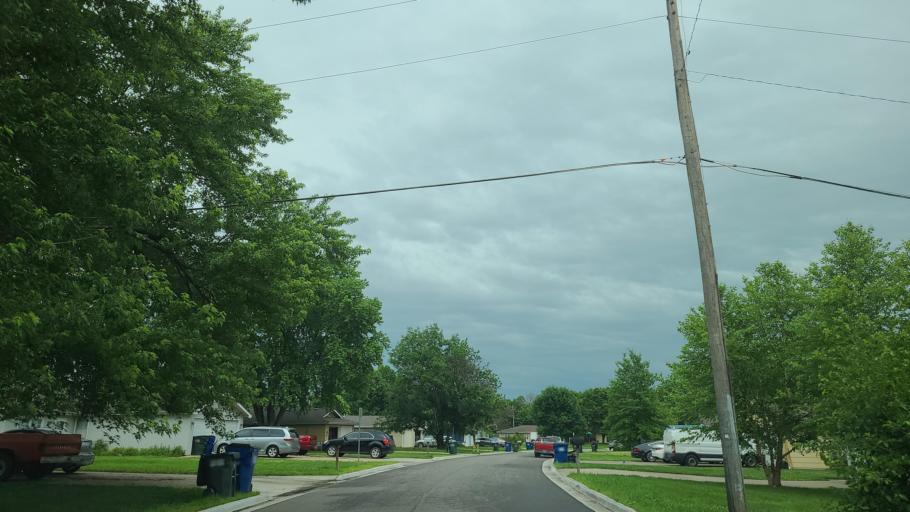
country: US
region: Kansas
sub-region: Douglas County
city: Lawrence
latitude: 38.9387
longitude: -95.2878
